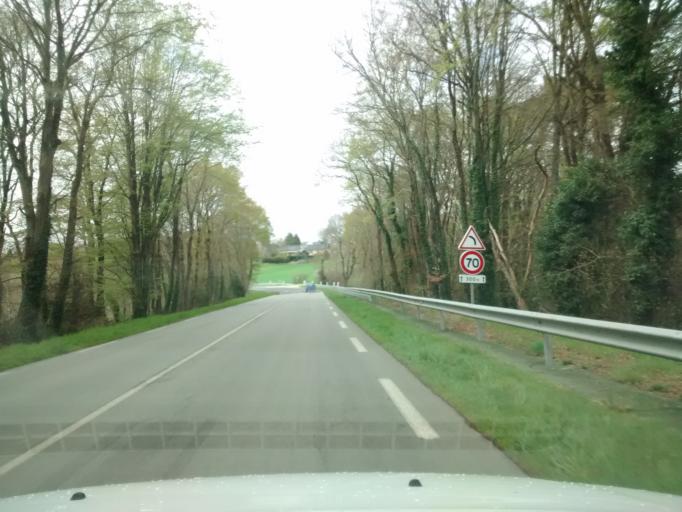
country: FR
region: Brittany
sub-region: Departement du Morbihan
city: Gestel
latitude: 47.7932
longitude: -3.4611
